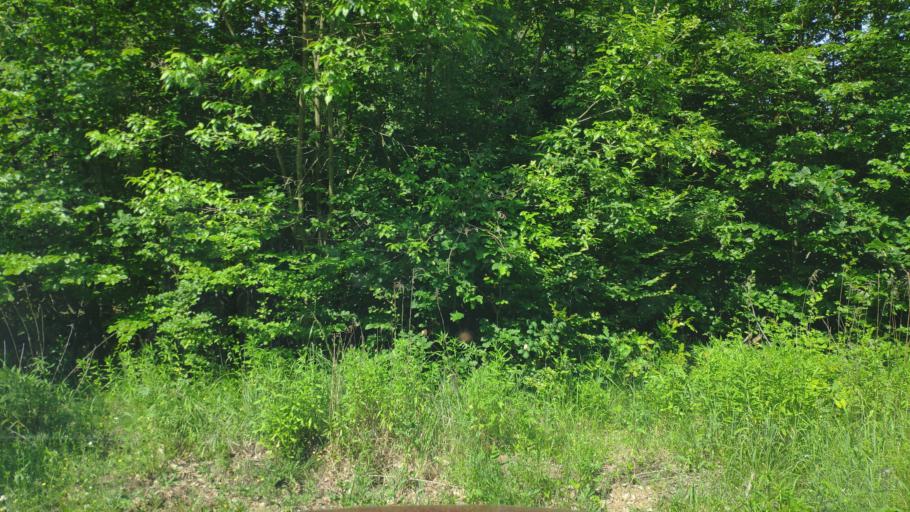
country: SK
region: Presovsky
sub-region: Okres Presov
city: Presov
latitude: 48.9708
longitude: 21.1499
